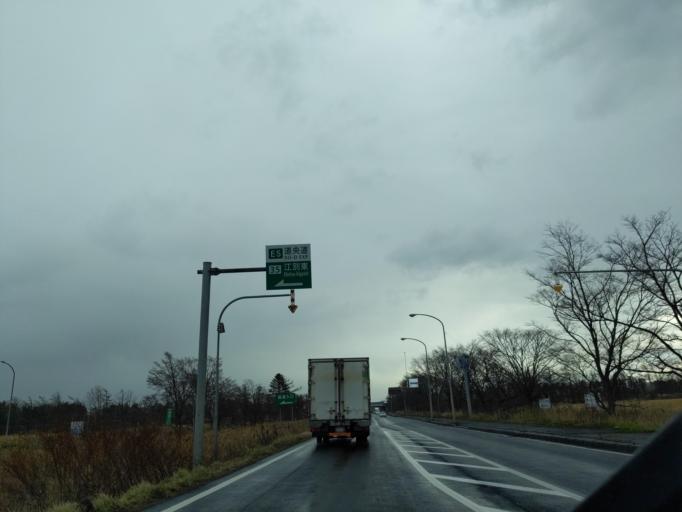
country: JP
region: Hokkaido
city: Ebetsu
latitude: 43.1070
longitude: 141.5945
